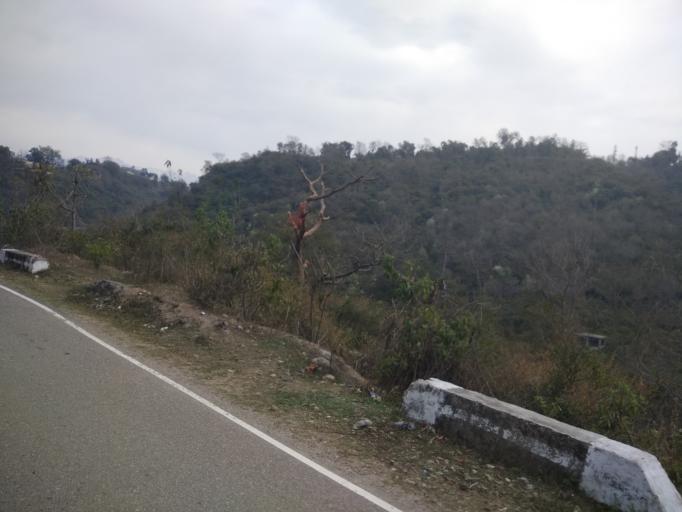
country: IN
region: Himachal Pradesh
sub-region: Kangra
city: Kotla
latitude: 32.2276
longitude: 76.0635
